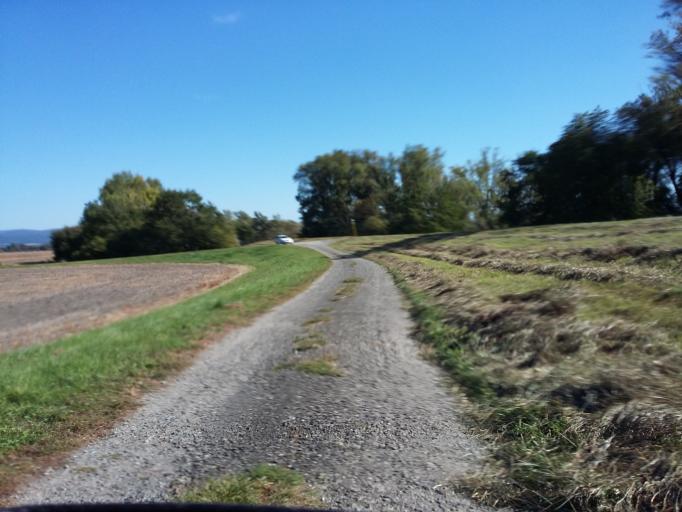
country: AT
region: Lower Austria
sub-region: Politischer Bezirk Ganserndorf
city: Marchegg
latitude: 48.2981
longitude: 16.9249
